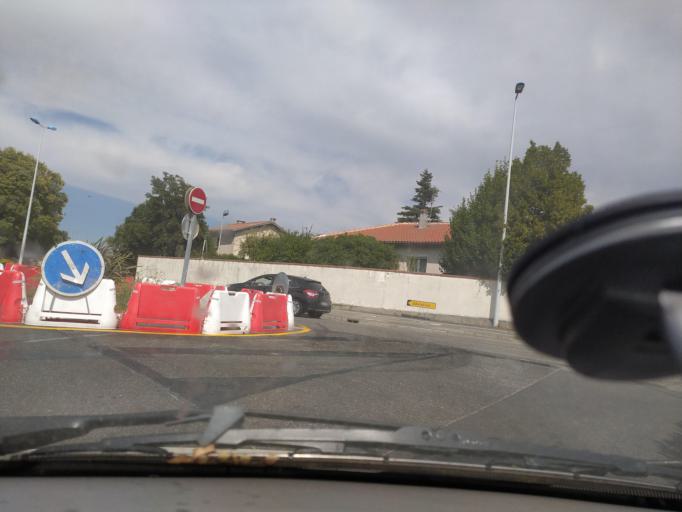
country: FR
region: Midi-Pyrenees
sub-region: Departement de la Haute-Garonne
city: Colomiers
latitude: 43.6039
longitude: 1.3358
